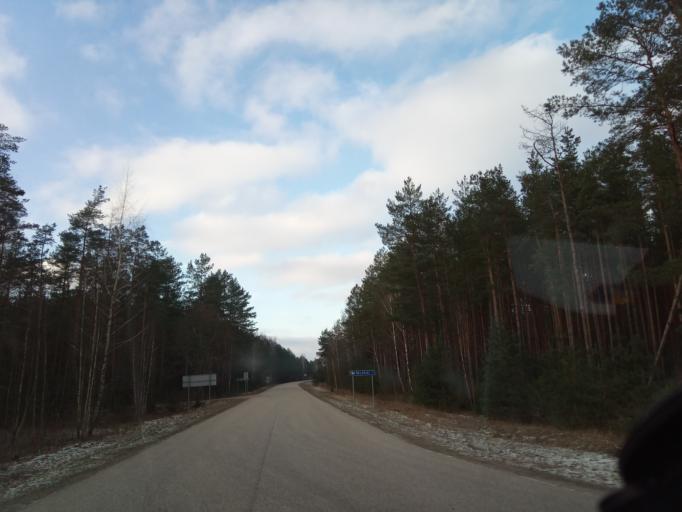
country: LT
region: Alytaus apskritis
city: Druskininkai
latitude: 53.9752
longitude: 24.2510
